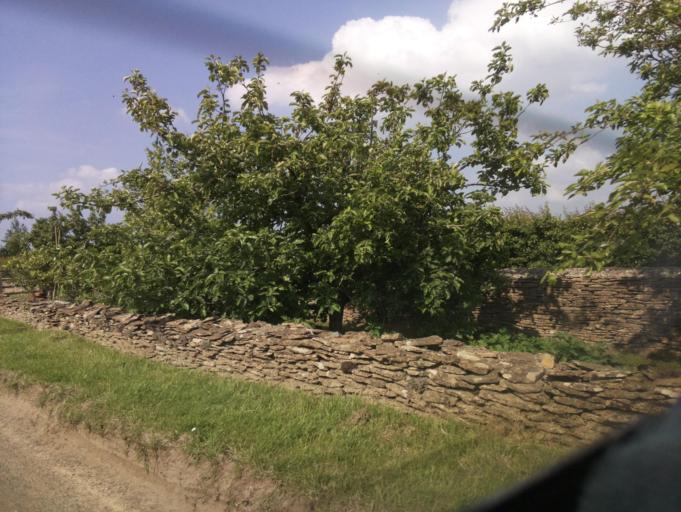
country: GB
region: England
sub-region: Wiltshire
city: Luckington
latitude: 51.5872
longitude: -2.2228
